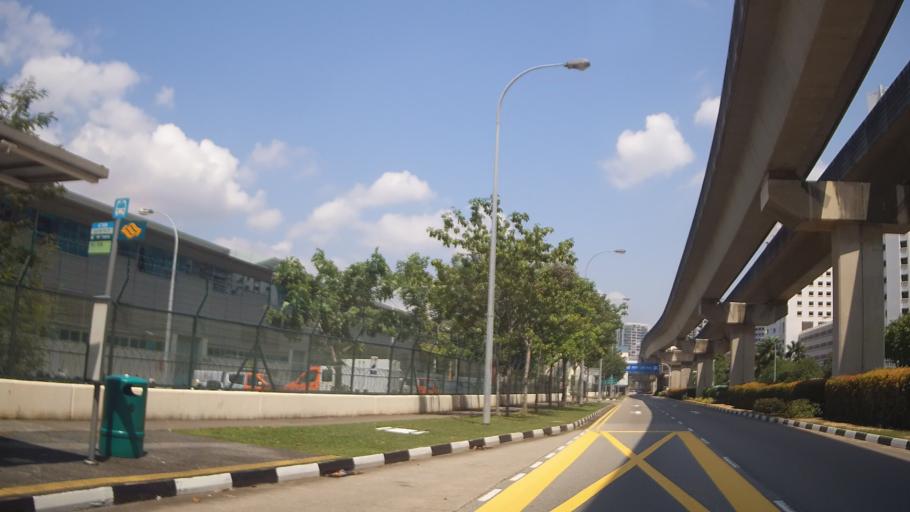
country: MY
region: Johor
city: Kampung Pasir Gudang Baru
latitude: 1.3882
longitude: 103.8875
